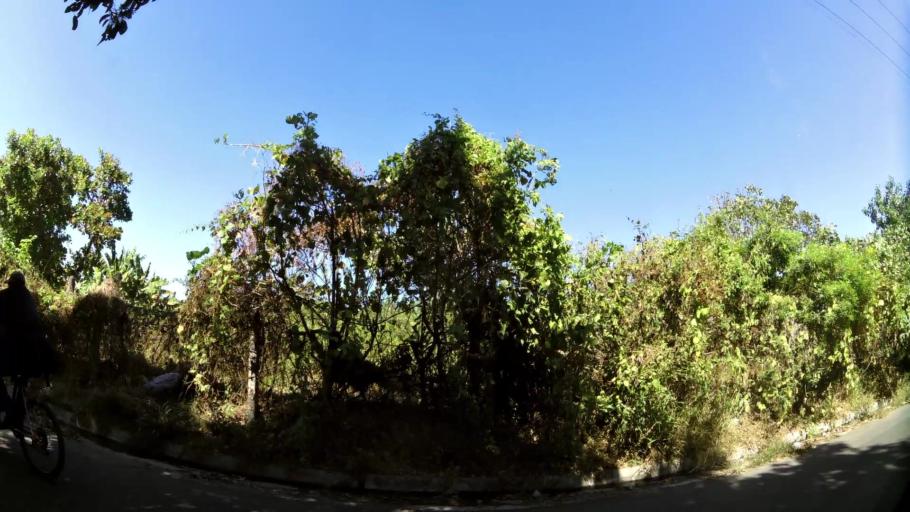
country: SV
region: La Libertad
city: Santa Tecla
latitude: 13.7340
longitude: -89.3803
